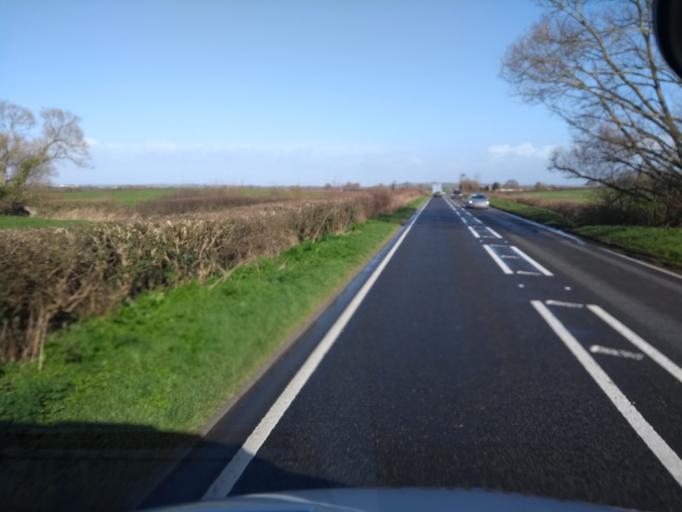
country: GB
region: England
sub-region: Somerset
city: Ilchester
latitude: 50.9820
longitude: -2.6752
